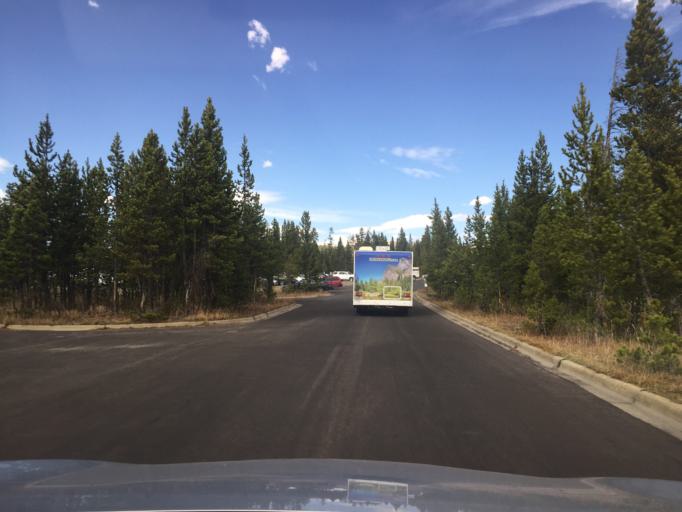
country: US
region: Montana
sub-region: Gallatin County
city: West Yellowstone
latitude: 44.7141
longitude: -110.4955
